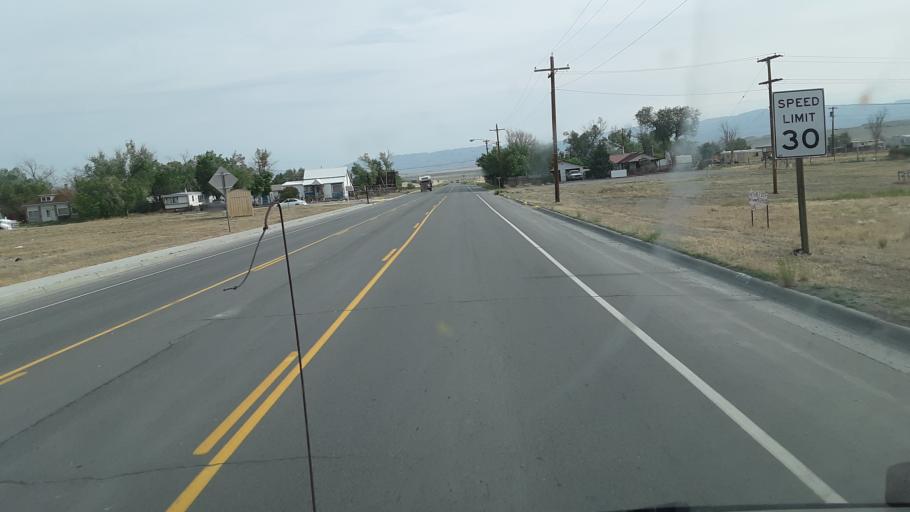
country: US
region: Wyoming
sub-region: Fremont County
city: Riverton
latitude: 43.2377
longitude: -108.1105
